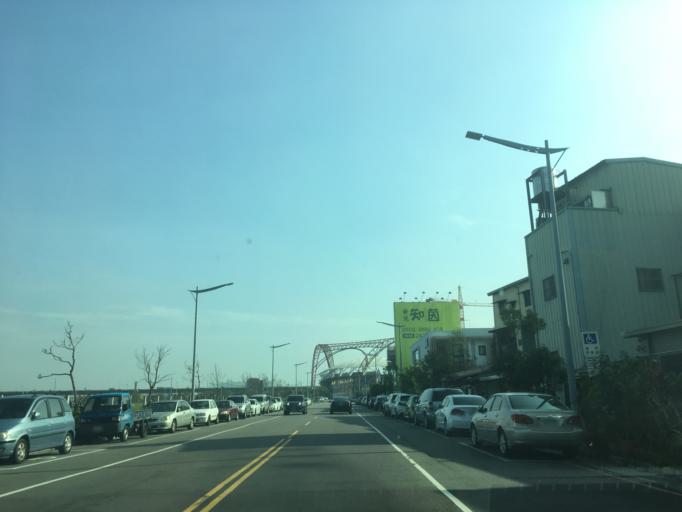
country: TW
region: Taiwan
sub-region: Taichung City
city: Taichung
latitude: 24.1952
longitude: 120.6825
